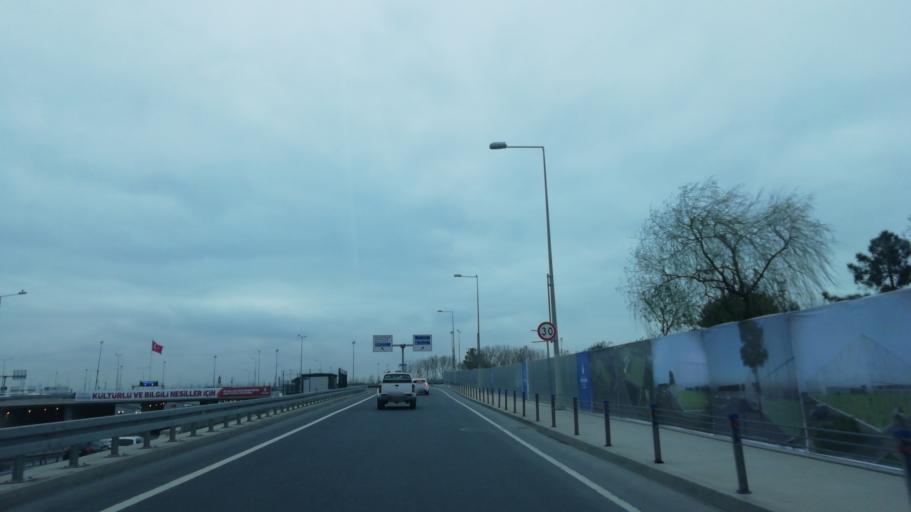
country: TR
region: Istanbul
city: Istanbul
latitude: 41.0013
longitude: 28.9415
